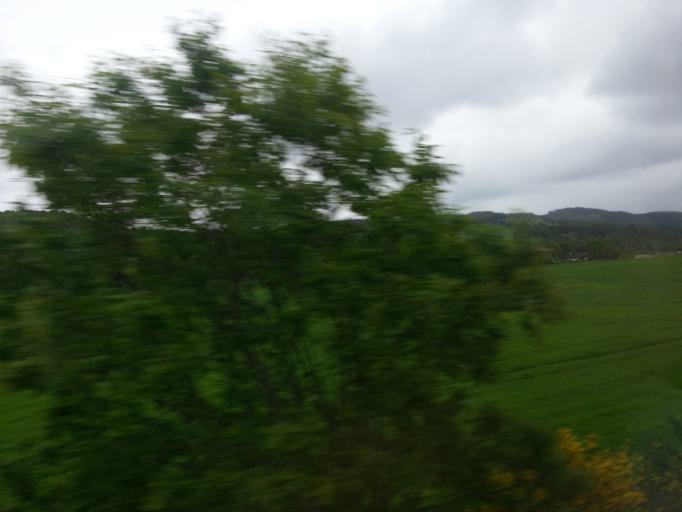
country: GB
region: Scotland
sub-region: Perth and Kinross
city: Pitlochry
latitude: 56.6177
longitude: -3.6351
